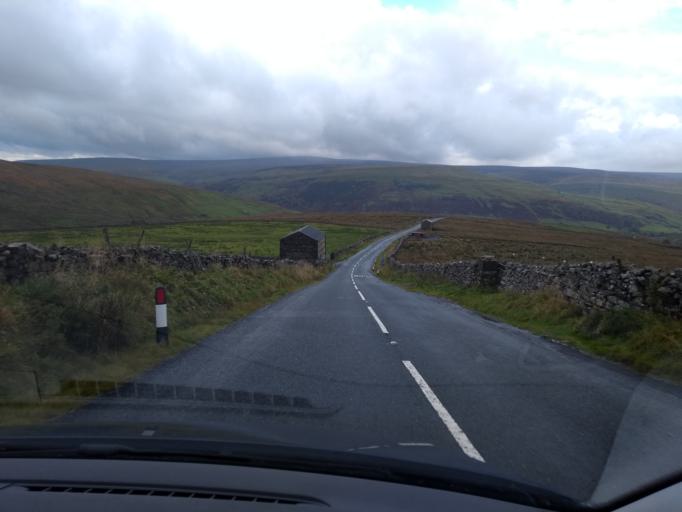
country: GB
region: England
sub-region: Cumbria
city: Kirkby Stephen
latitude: 54.3711
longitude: -2.1856
